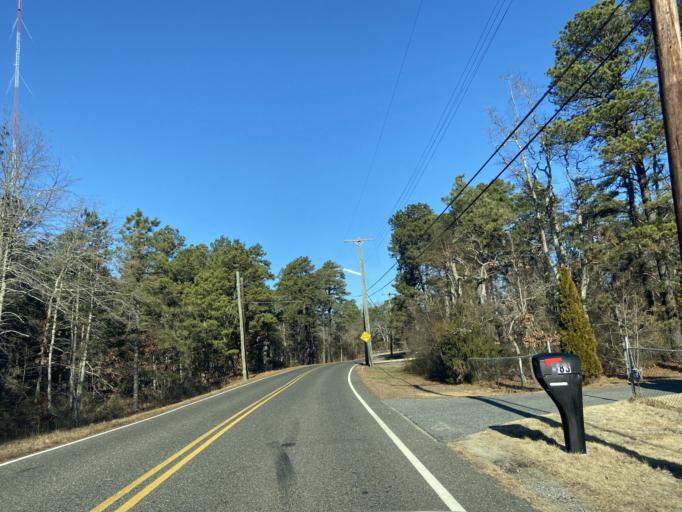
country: US
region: New Jersey
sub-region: Cumberland County
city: Vineland
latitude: 39.4969
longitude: -75.0736
